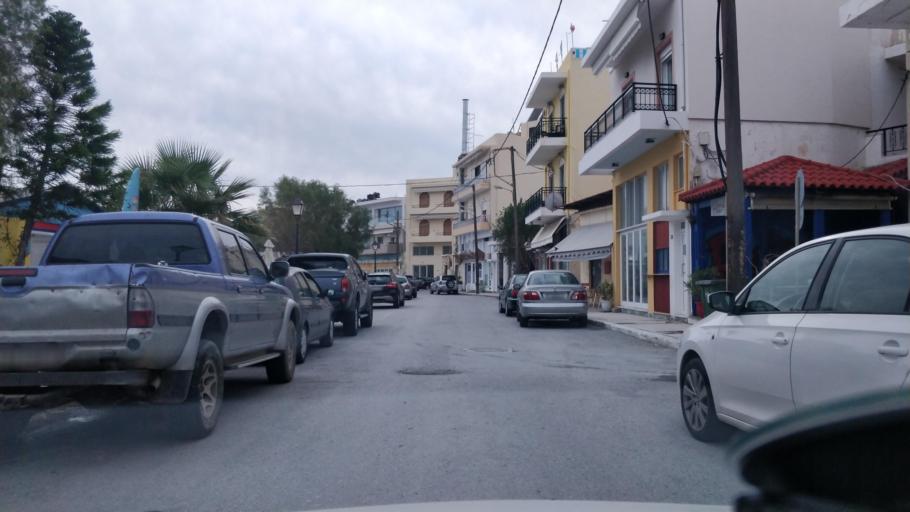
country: GR
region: Crete
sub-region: Nomos Lasithiou
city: Ierapetra
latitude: 35.0056
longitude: 25.7377
